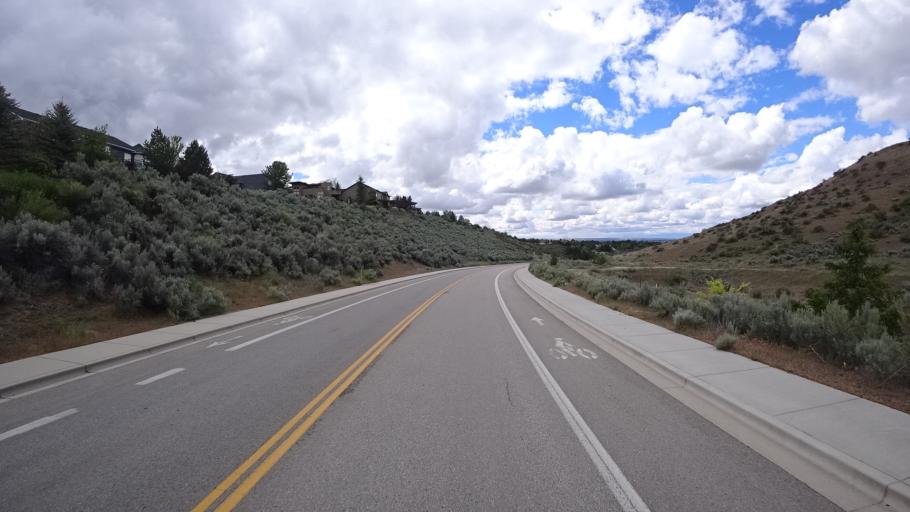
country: US
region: Idaho
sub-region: Ada County
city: Boise
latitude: 43.6576
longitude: -116.1895
